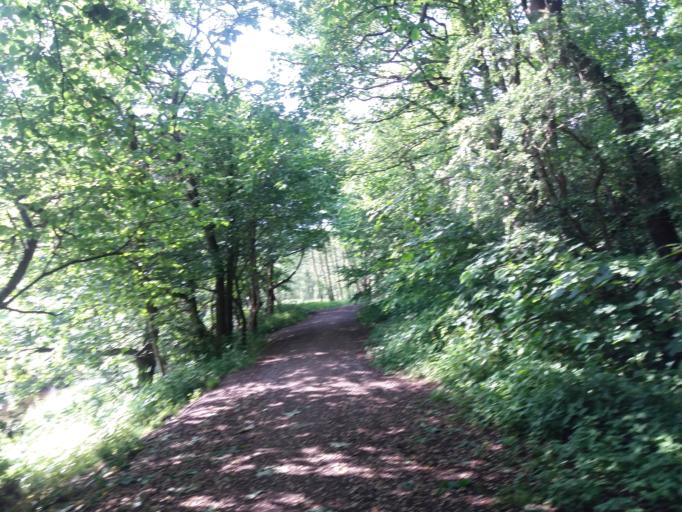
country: GB
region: England
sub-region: Lancashire
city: Coppull
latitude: 53.6479
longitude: -2.6562
